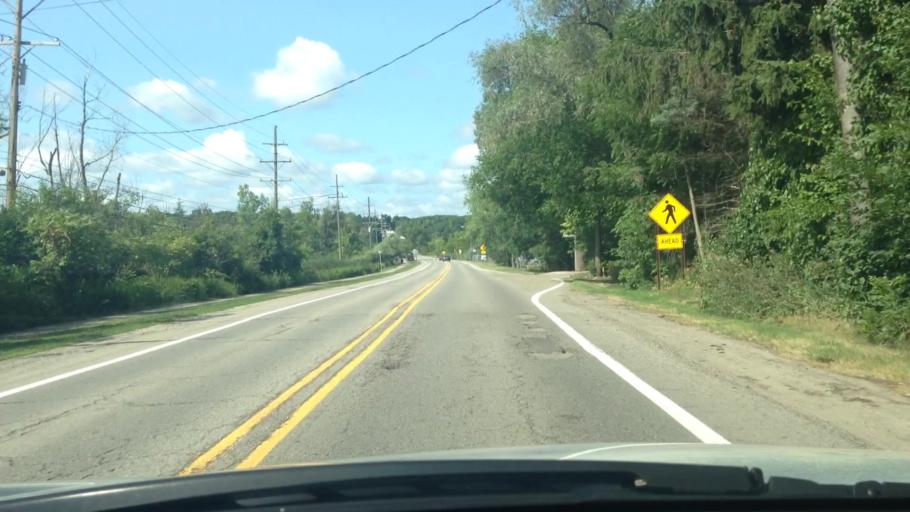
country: US
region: Michigan
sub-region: Oakland County
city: Clarkston
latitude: 42.7323
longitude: -83.4237
